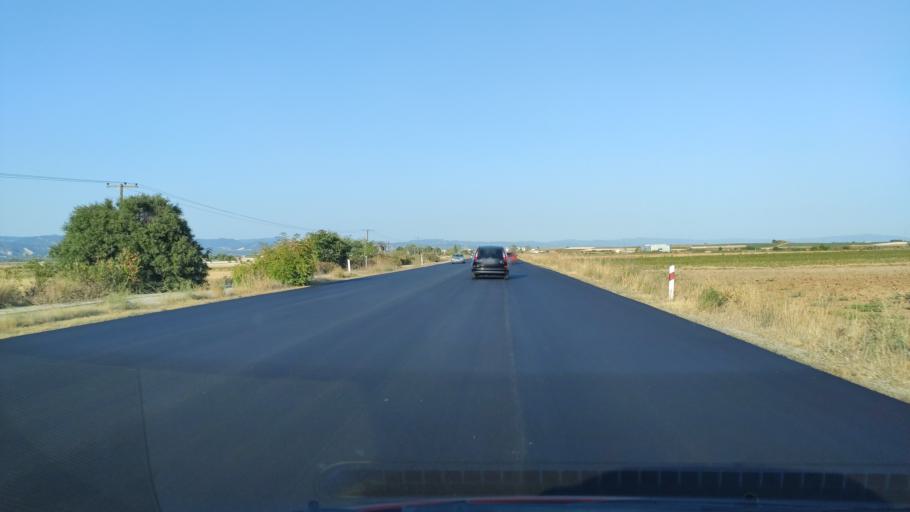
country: GR
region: East Macedonia and Thrace
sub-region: Nomos Rodopis
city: Komotini
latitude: 41.0993
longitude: 25.3150
